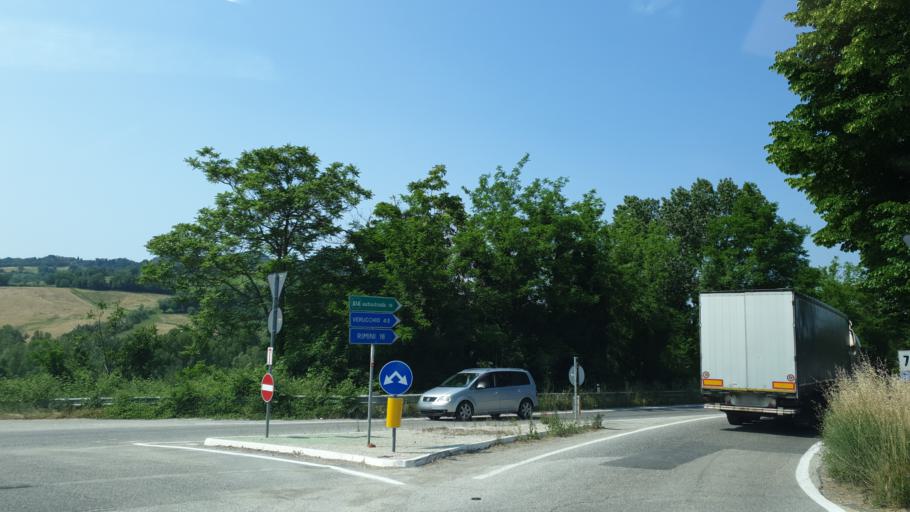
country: SM
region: Acquaviva
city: Acquaviva
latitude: 43.9615
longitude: 12.4019
